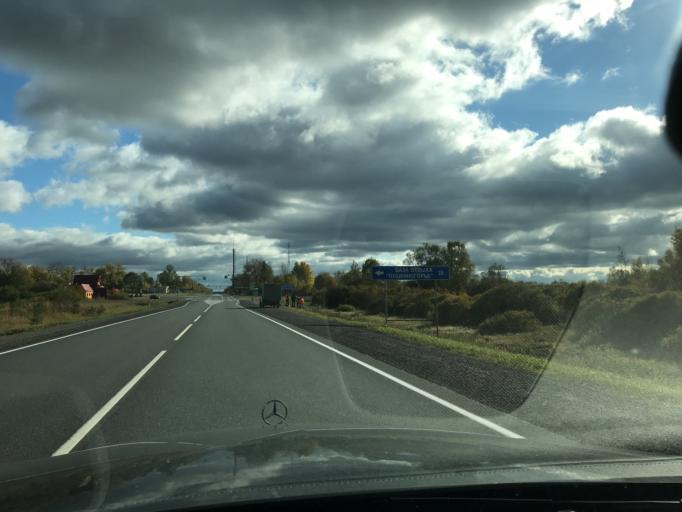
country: RU
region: Pskov
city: Pushkinskiye Gory
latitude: 57.0570
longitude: 28.5775
